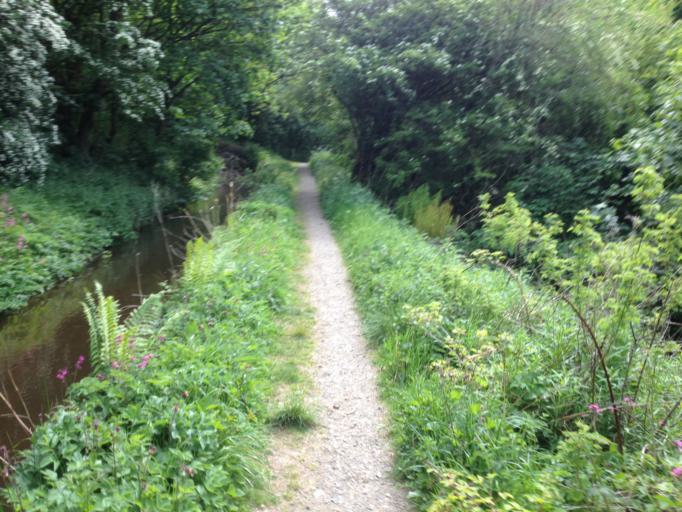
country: GB
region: Scotland
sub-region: West Lothian
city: East Calder
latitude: 55.9087
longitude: -3.4532
